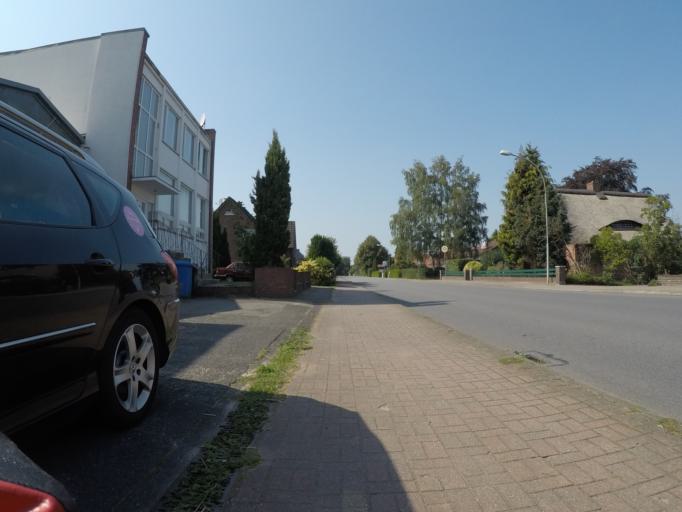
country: DE
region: Schleswig-Holstein
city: Sievershutten
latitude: 53.8416
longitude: 10.1055
